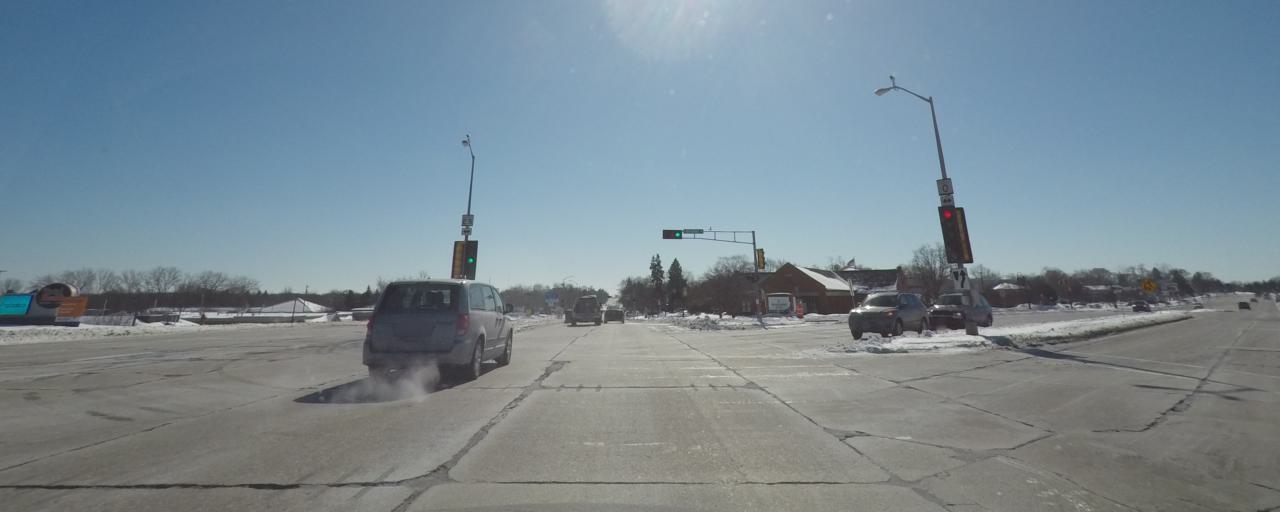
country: US
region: Wisconsin
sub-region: Waukesha County
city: New Berlin
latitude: 42.9763
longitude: -88.1086
